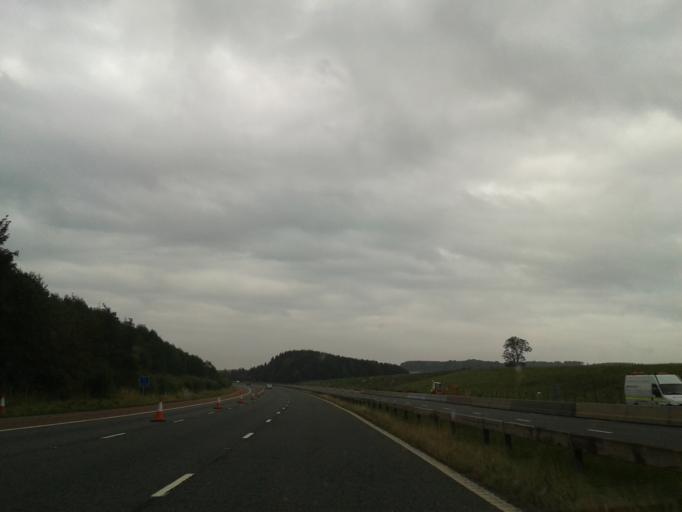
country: GB
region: England
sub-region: Cumbria
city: Penrith
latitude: 54.5882
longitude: -2.7012
